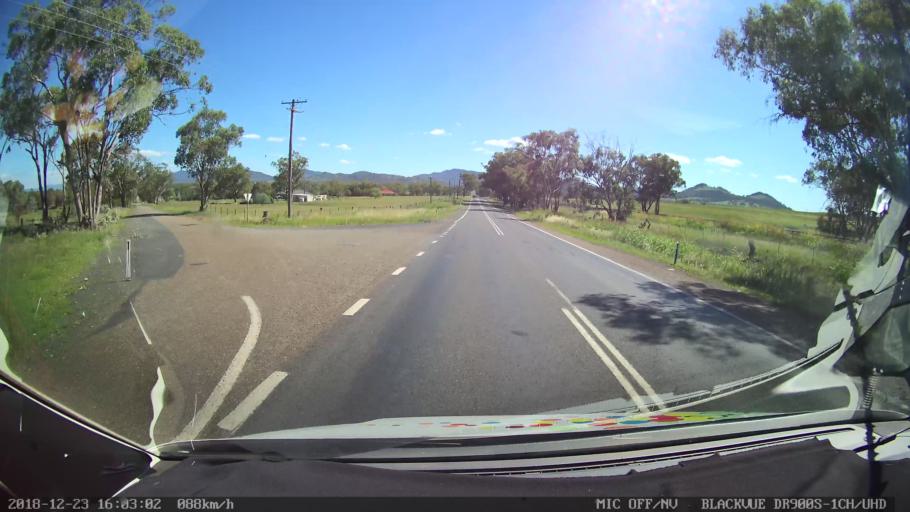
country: AU
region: New South Wales
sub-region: Tamworth Municipality
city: Phillip
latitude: -31.2387
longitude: 150.8042
